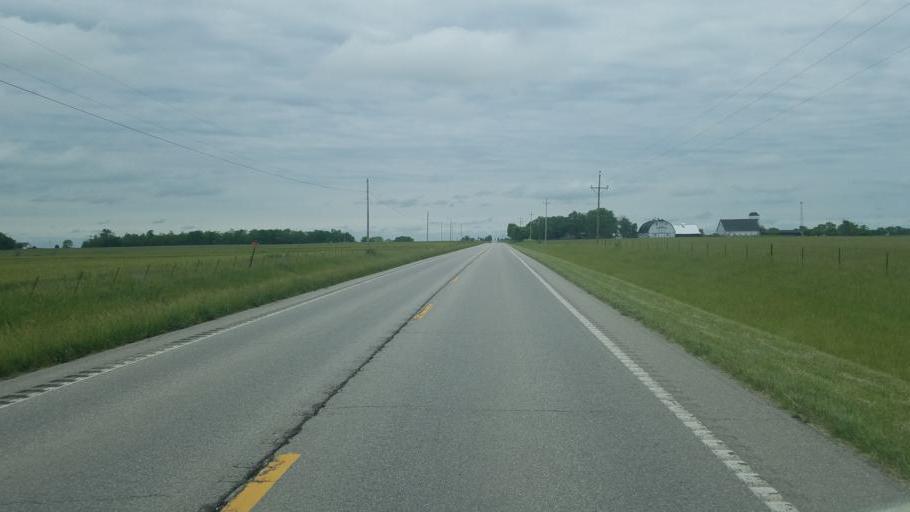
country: US
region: Missouri
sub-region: Morgan County
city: Versailles
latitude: 38.4826
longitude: -92.8085
